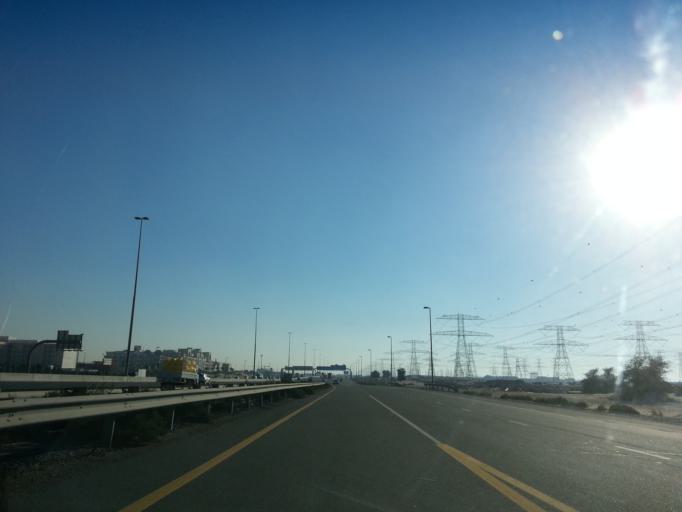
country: AE
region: Dubai
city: Dubai
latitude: 25.0736
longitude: 55.2071
